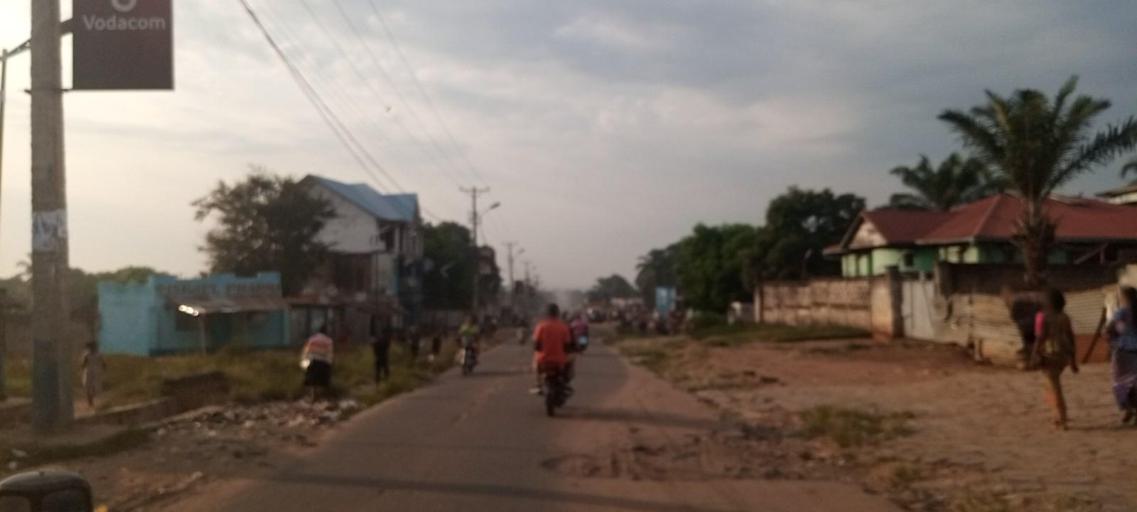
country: CD
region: Kasai-Oriental
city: Mbuji-Mayi
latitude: -6.1247
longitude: 23.5979
